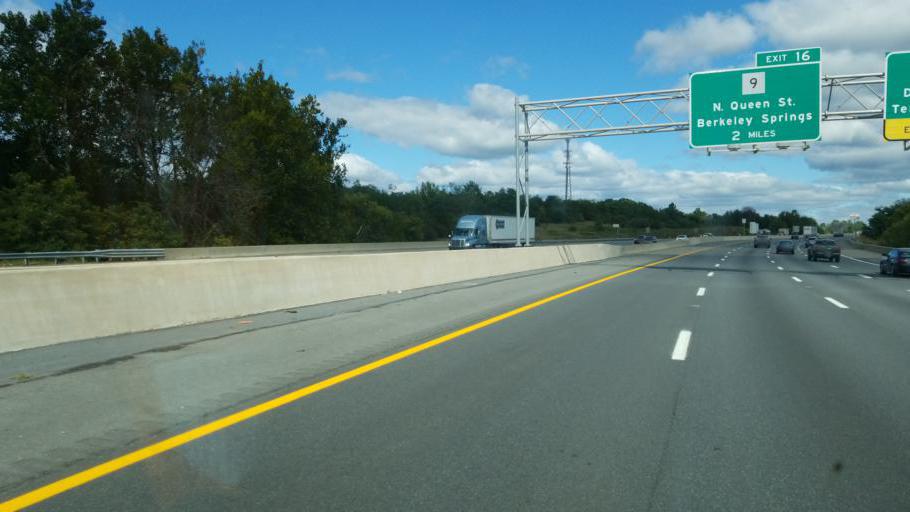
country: US
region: West Virginia
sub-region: Berkeley County
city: Martinsburg
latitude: 39.4698
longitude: -77.9893
